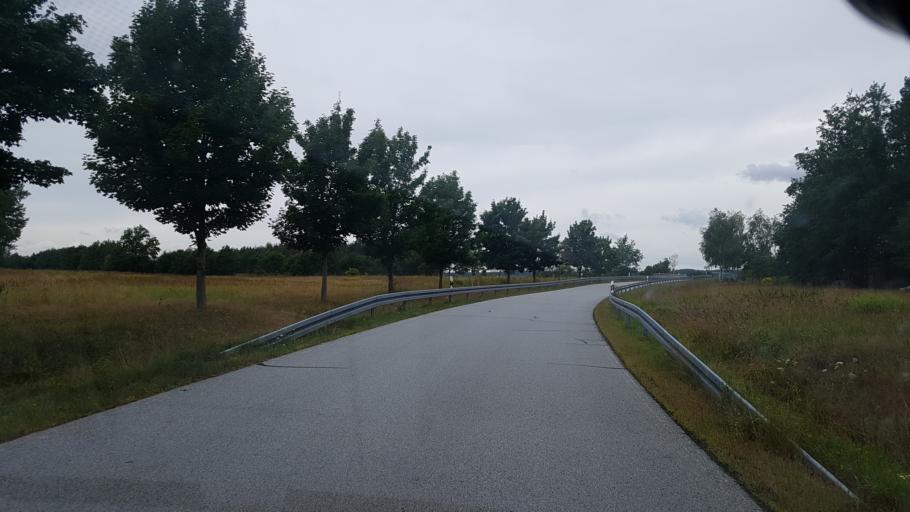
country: DE
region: Saxony
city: Konigshain
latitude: 51.2121
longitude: 14.8024
